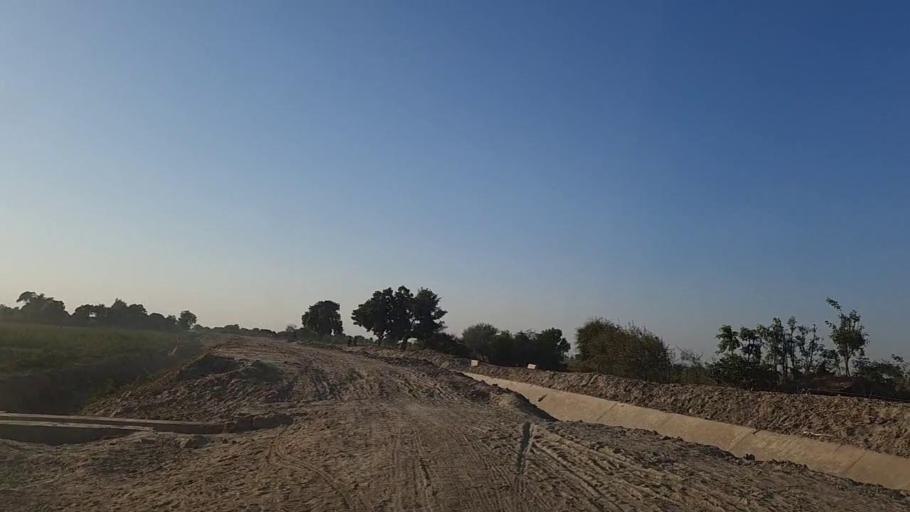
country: PK
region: Sindh
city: Naukot
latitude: 25.0048
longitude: 69.3922
